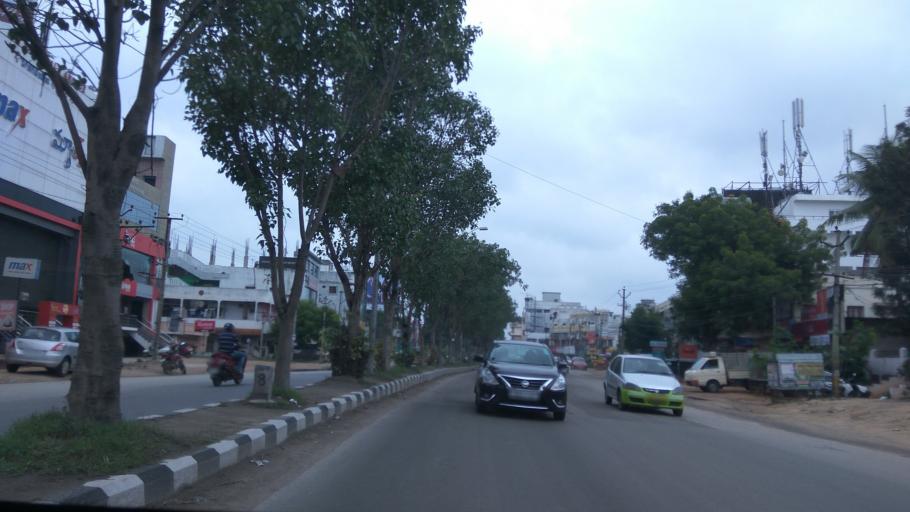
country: IN
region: Telangana
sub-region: Rangareddi
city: Secunderabad
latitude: 17.4790
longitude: 78.5594
